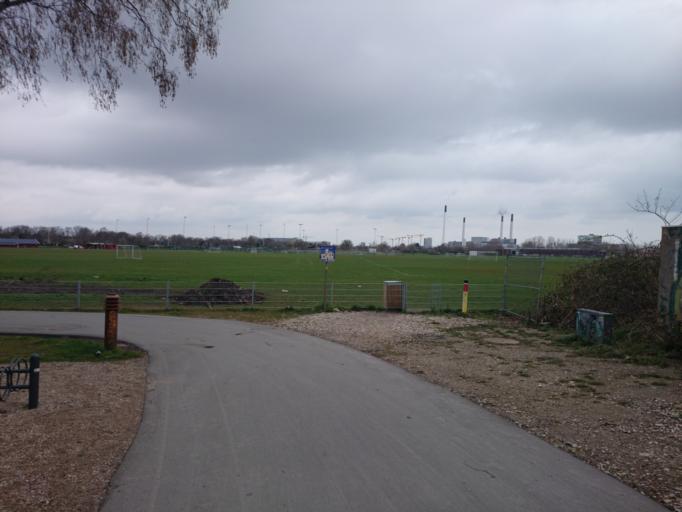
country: DK
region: Capital Region
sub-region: Kobenhavn
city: Christianshavn
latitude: 55.6697
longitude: 12.6112
